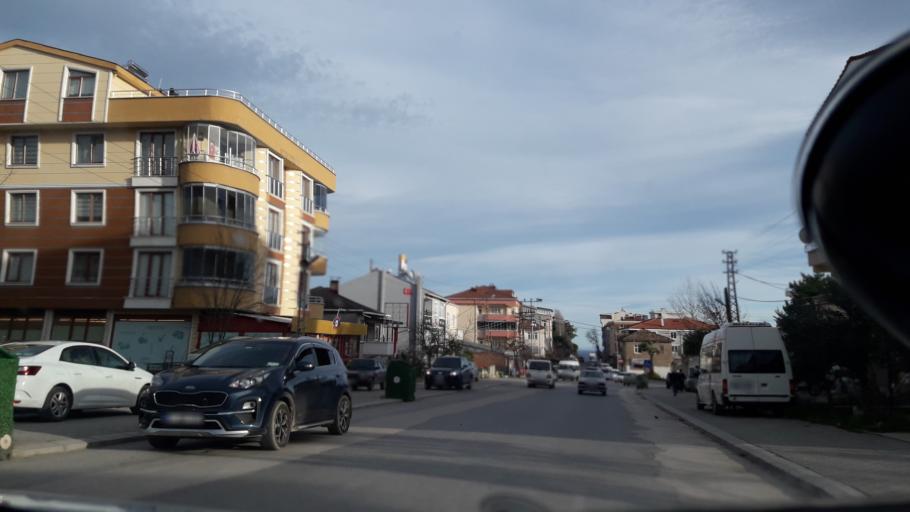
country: TR
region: Sinop
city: Gerze
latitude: 41.8065
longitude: 35.1889
